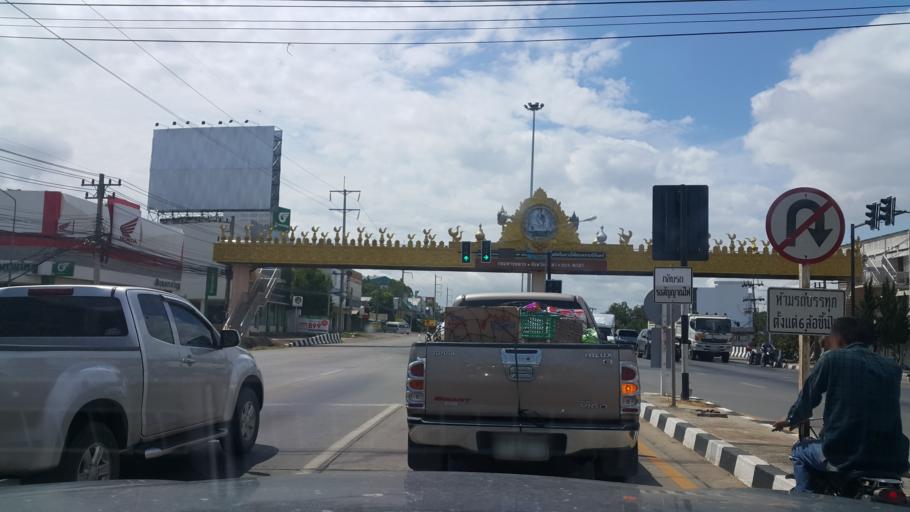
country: TH
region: Phayao
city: Phayao
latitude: 19.1714
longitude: 99.9064
